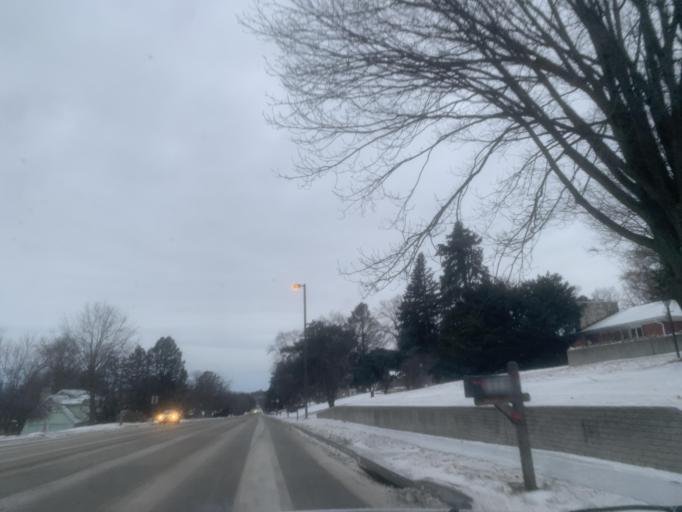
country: US
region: Nebraska
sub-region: Douglas County
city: Ralston
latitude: 41.2444
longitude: -96.0527
